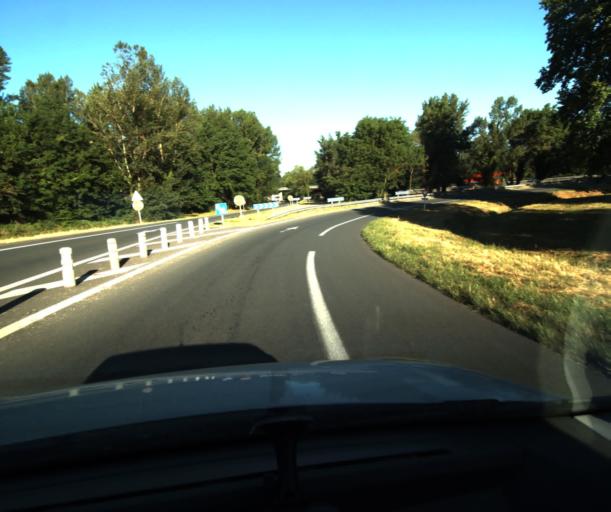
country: FR
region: Midi-Pyrenees
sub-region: Departement du Tarn-et-Garonne
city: Castelsarrasin
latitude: 44.0516
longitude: 1.0962
